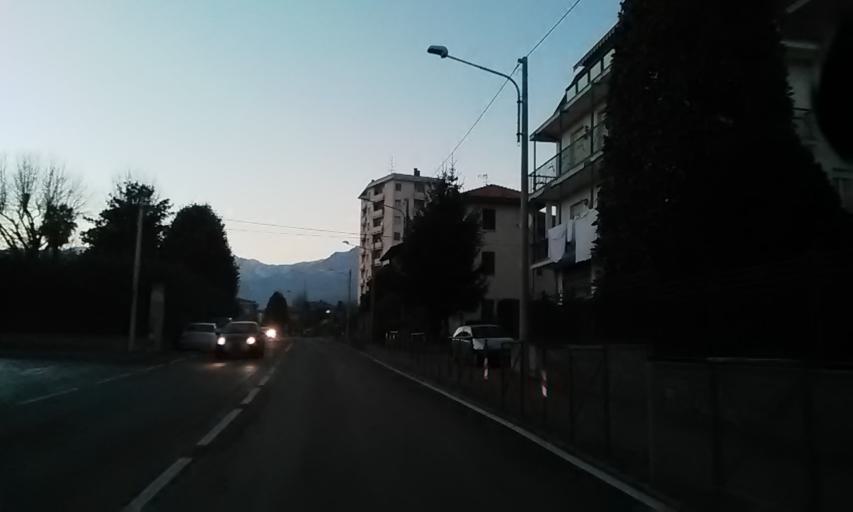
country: IT
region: Piedmont
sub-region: Provincia di Biella
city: Vigliano Biellese
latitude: 45.5596
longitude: 8.0917
